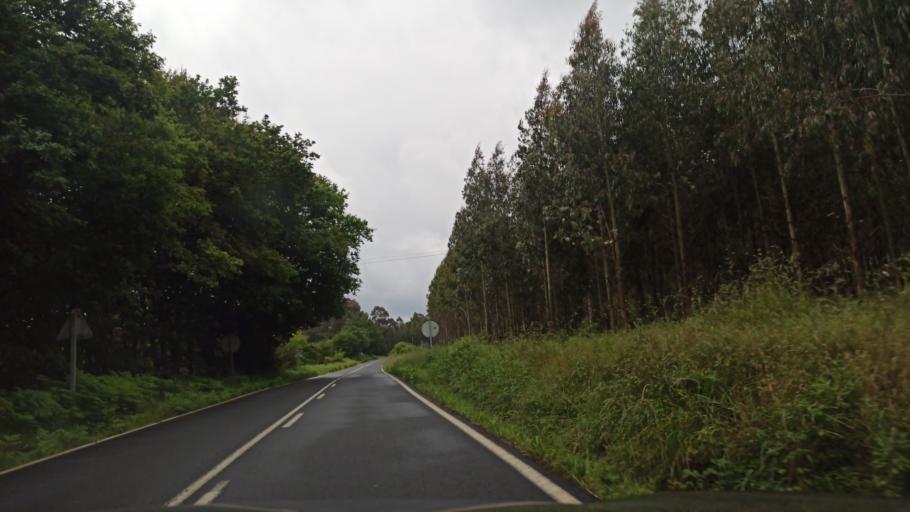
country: ES
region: Galicia
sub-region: Provincia da Coruna
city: Santiso
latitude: 42.7836
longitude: -8.0436
